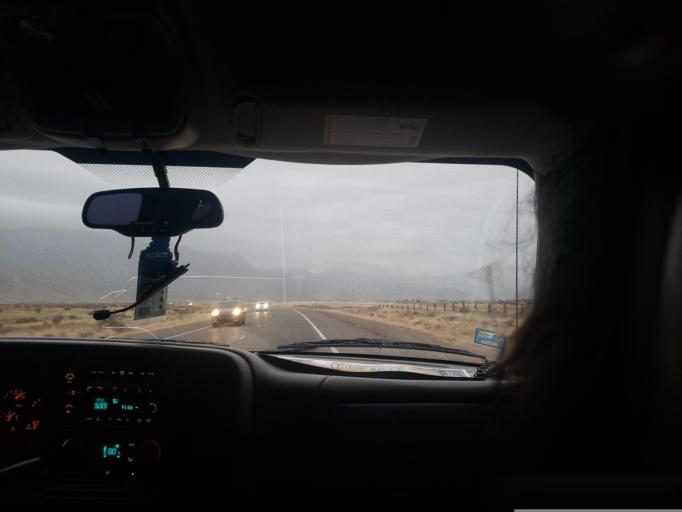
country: US
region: New Mexico
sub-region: Bernalillo County
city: Sandia Heights
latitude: 35.2016
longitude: -106.5518
